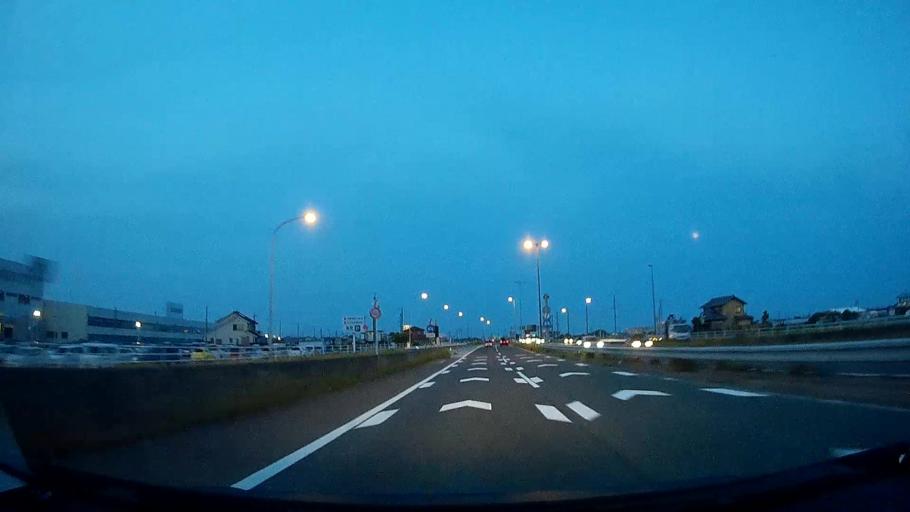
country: JP
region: Shizuoka
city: Hamamatsu
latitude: 34.6805
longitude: 137.6679
